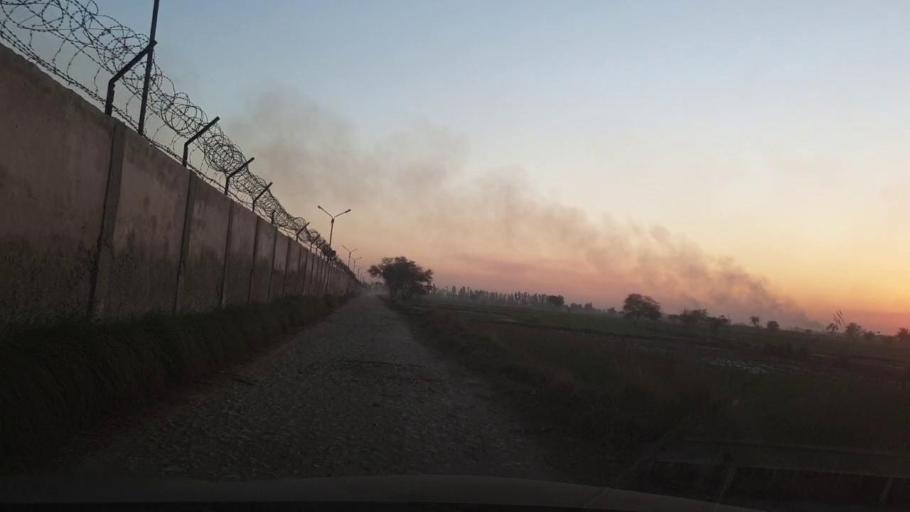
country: PK
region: Sindh
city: Ghotki
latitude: 28.0522
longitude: 69.3599
